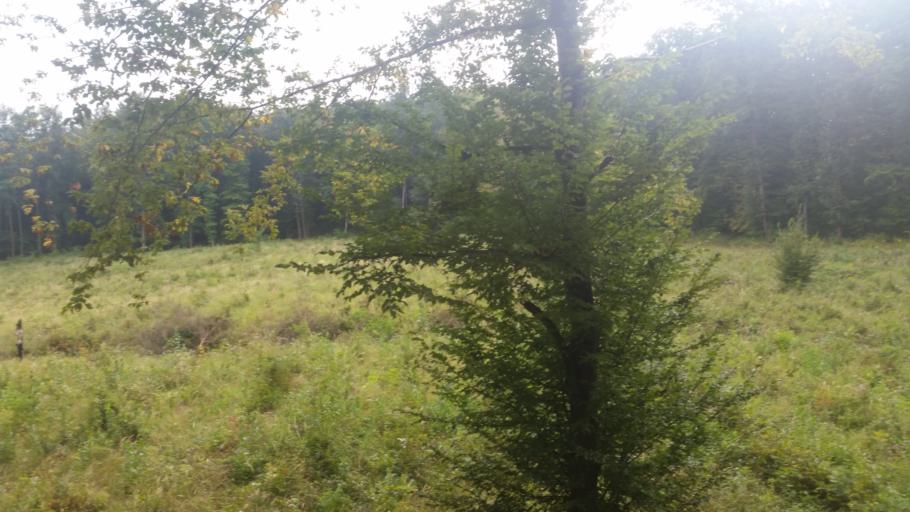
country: HU
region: Baranya
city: Sasd
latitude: 46.1835
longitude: 18.1190
